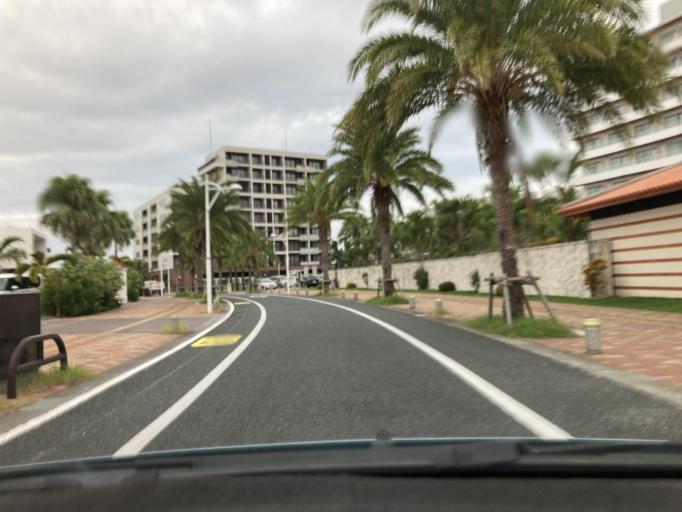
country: JP
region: Okinawa
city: Chatan
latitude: 26.3189
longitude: 127.7543
